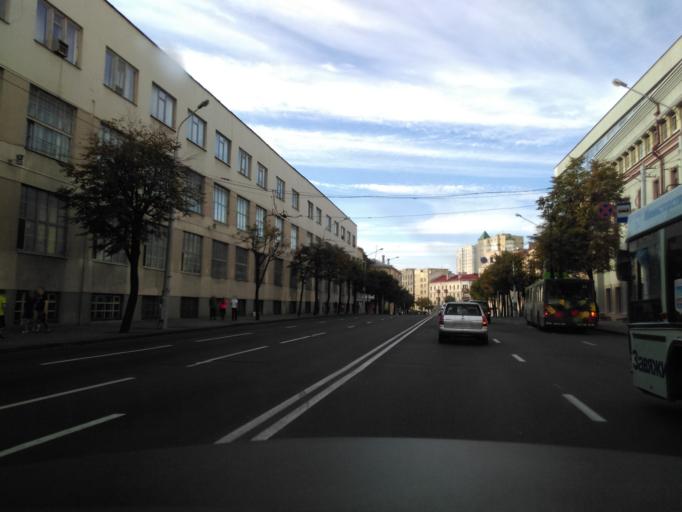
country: BY
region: Minsk
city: Minsk
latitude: 53.9229
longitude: 27.6005
